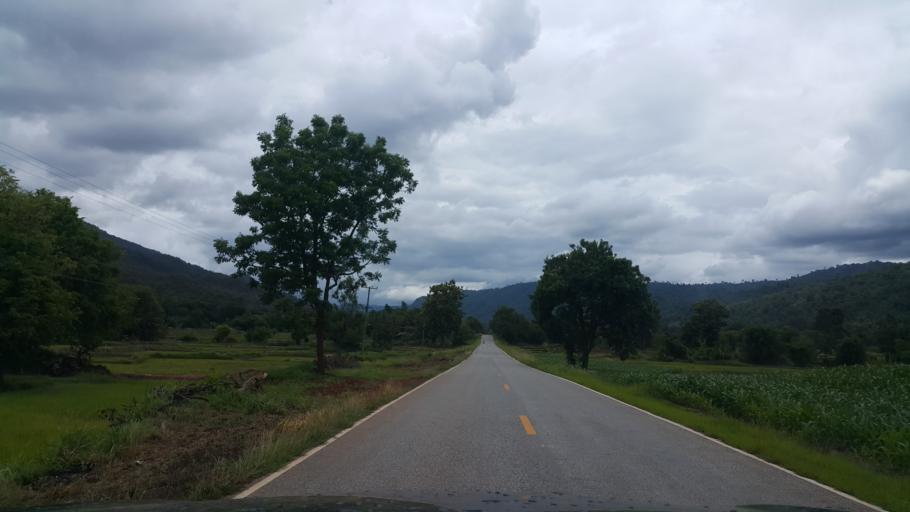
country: TH
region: Phitsanulok
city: Chat Trakan
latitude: 17.3251
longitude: 100.6926
